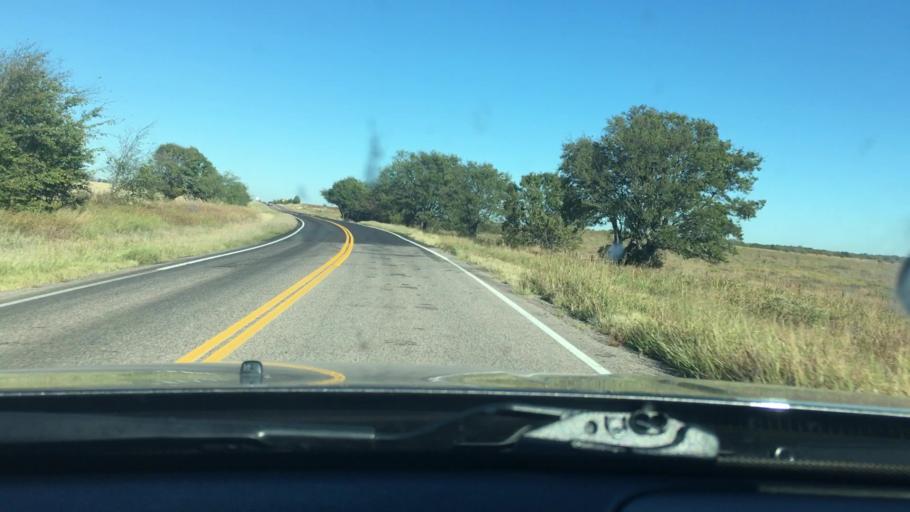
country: US
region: Oklahoma
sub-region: Johnston County
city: Tishomingo
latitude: 34.1642
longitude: -96.7072
